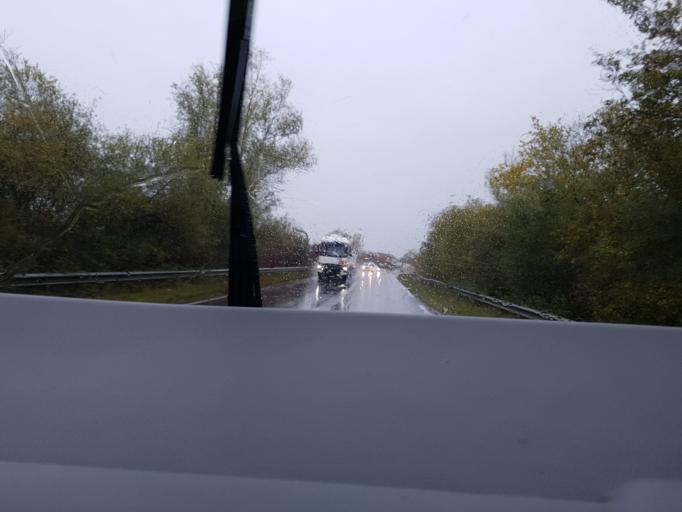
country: FR
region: Aquitaine
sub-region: Departement de la Gironde
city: Saint-Vincent-de-Paul
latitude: 44.9600
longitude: -0.4731
